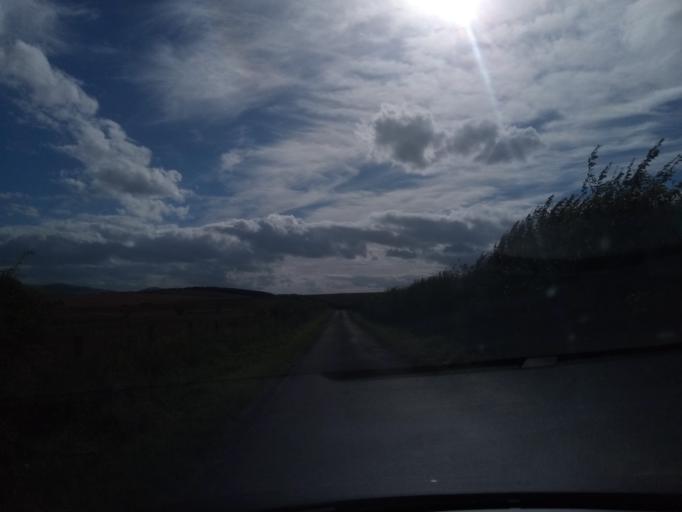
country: GB
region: England
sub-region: Northumberland
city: Kirknewton
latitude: 55.6101
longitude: -2.1770
